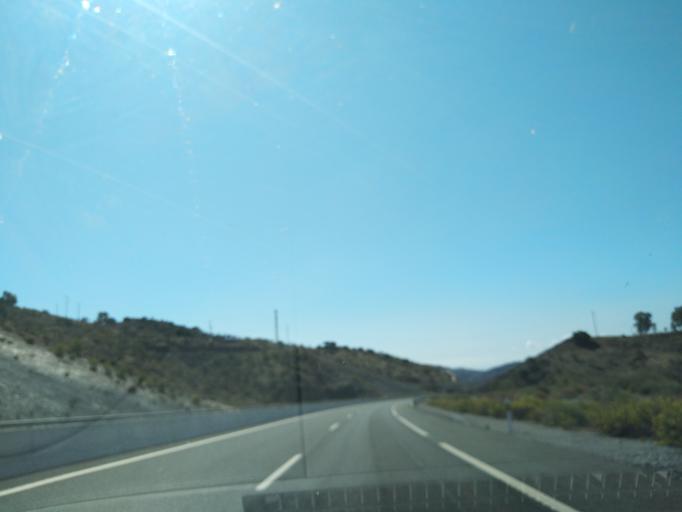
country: ES
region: Andalusia
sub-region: Provincia de Malaga
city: Almogia
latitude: 36.8161
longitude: -4.4701
